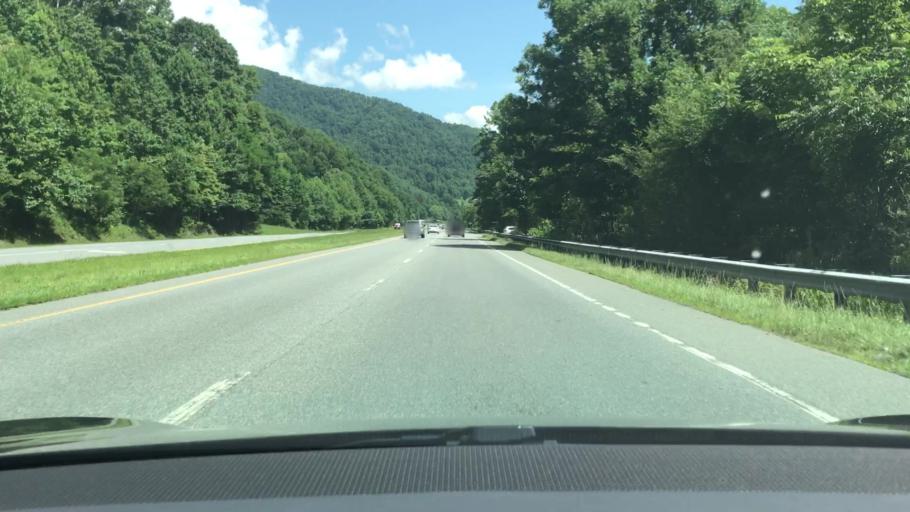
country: US
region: North Carolina
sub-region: Jackson County
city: Sylva
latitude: 35.2815
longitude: -83.2862
